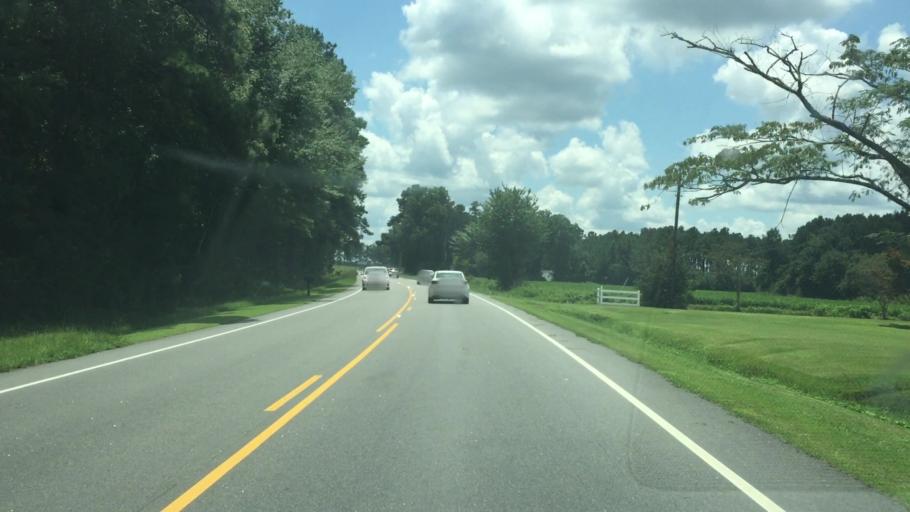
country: US
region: North Carolina
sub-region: Columbus County
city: Tabor City
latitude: 34.1832
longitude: -78.8388
